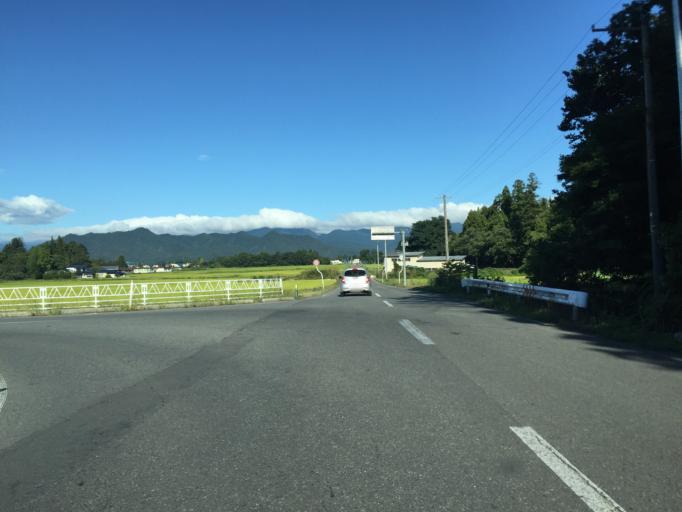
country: JP
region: Yamagata
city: Yonezawa
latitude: 37.9514
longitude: 140.1433
